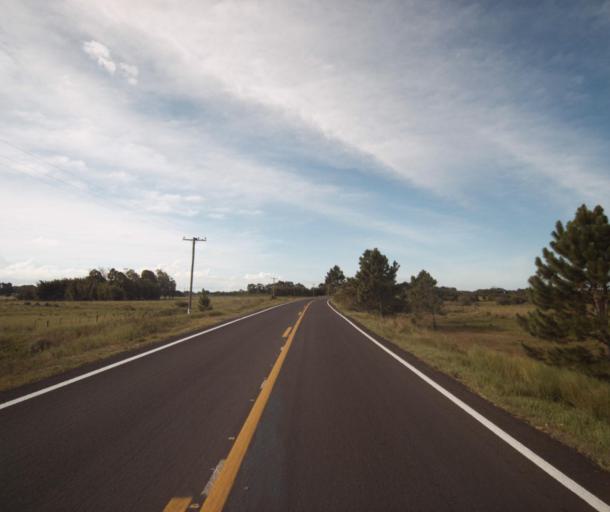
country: BR
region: Rio Grande do Sul
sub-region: Tapes
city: Tapes
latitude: -31.3280
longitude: -51.1264
